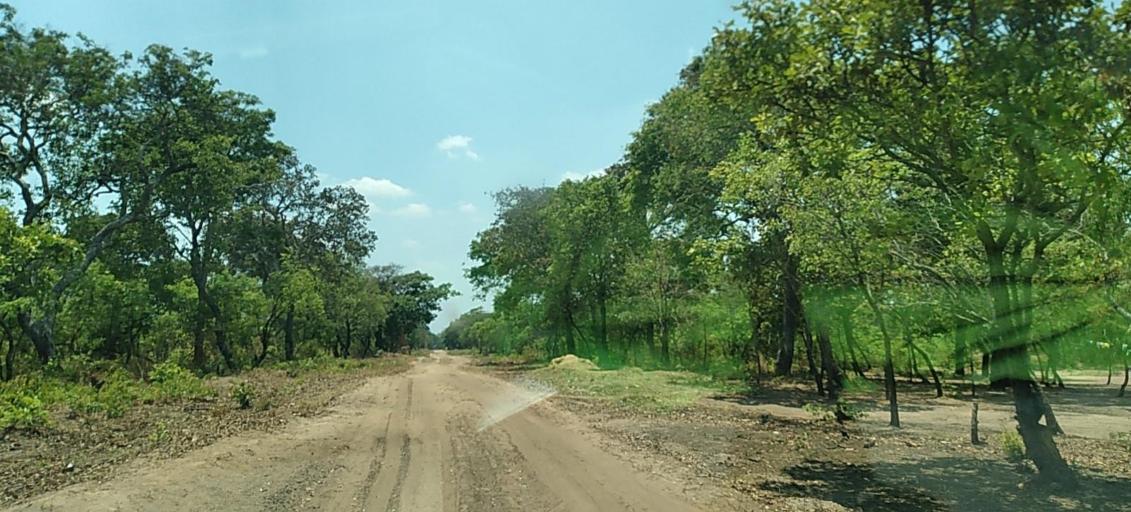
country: CD
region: Katanga
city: Kolwezi
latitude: -11.3822
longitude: 25.2186
